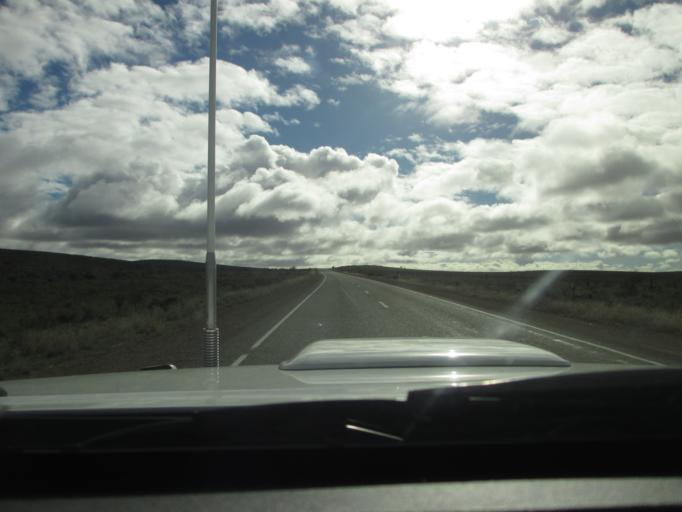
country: AU
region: South Australia
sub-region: Flinders Ranges
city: Quorn
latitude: -32.1912
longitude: 138.5346
